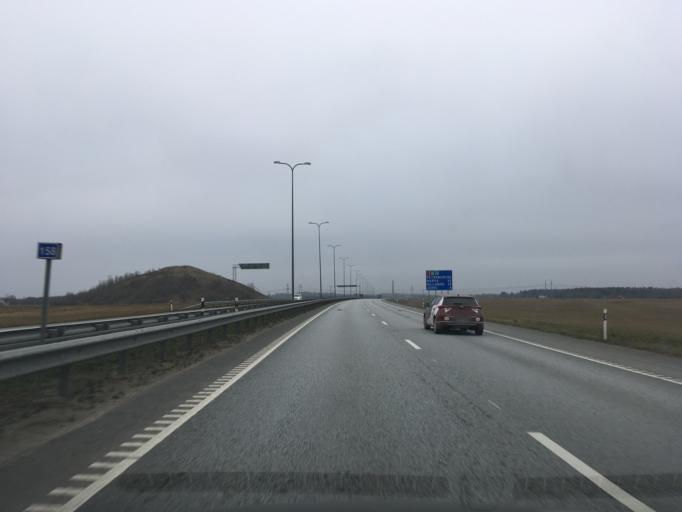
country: EE
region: Ida-Virumaa
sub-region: Kohtla-Jaerve linn
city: Kohtla-Jarve
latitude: 59.3986
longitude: 27.3327
